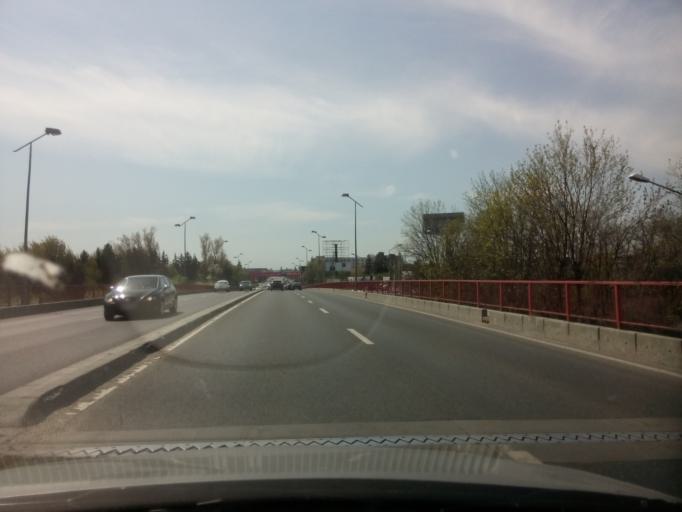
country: RO
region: Ilfov
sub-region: Comuna Otopeni
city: Otopeni
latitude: 44.5722
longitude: 26.0699
